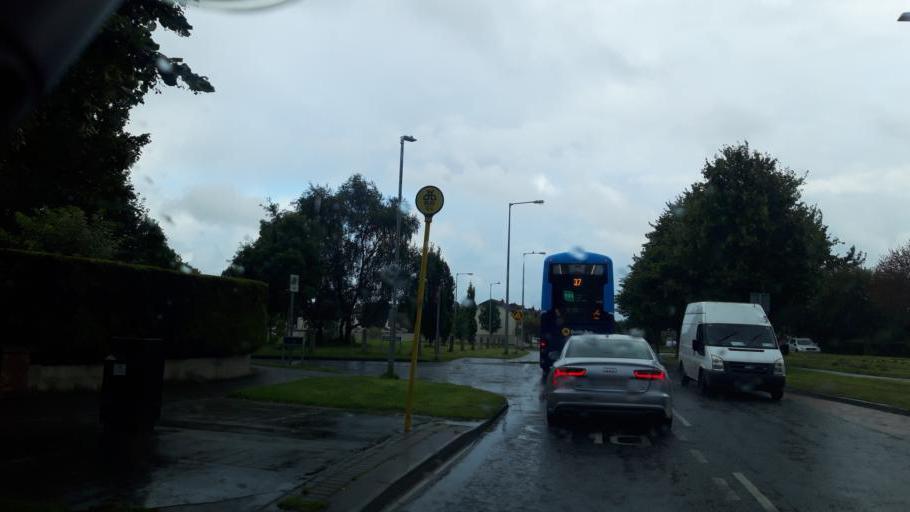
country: IE
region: Leinster
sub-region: Fingal County
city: Blanchardstown
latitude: 53.3762
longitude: -6.3828
